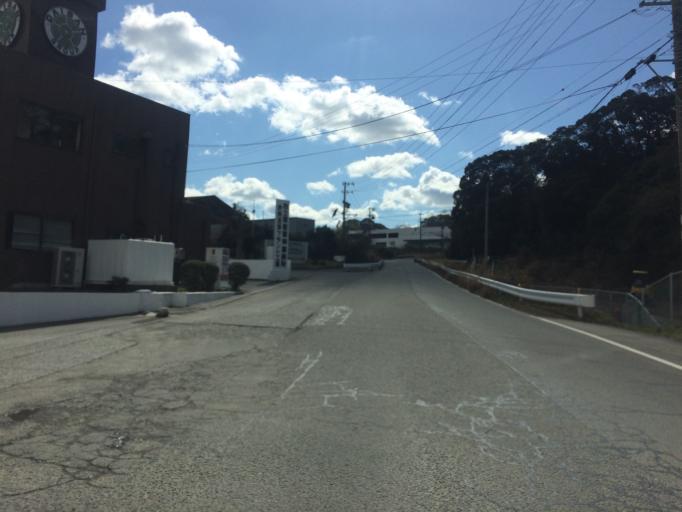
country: JP
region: Shizuoka
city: Shimada
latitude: 34.7736
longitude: 138.1994
